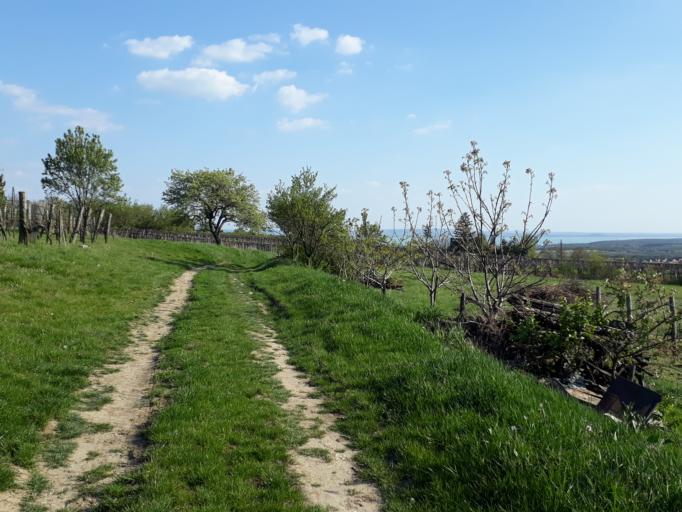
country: HU
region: Veszprem
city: Zanka
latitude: 46.9173
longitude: 17.6823
